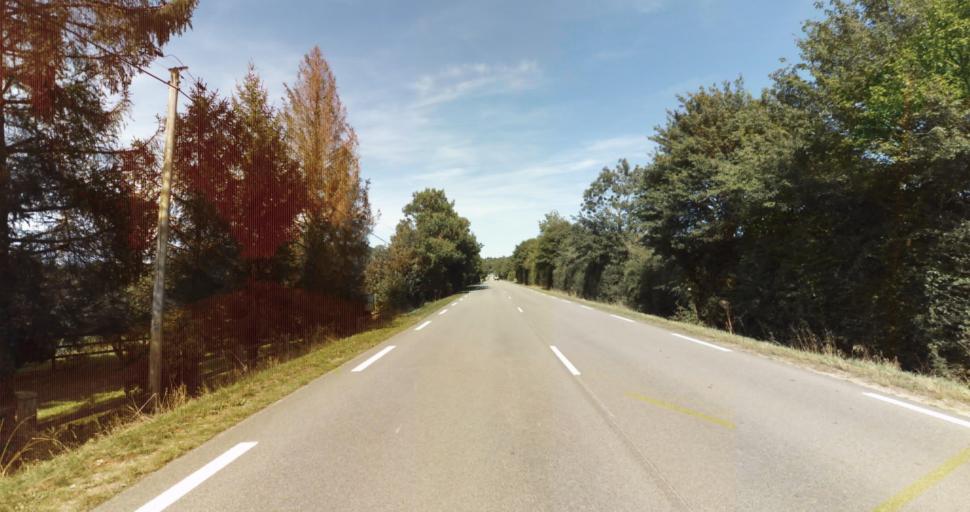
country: FR
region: Lower Normandy
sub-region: Departement de l'Orne
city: Gace
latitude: 48.7207
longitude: 0.2309
